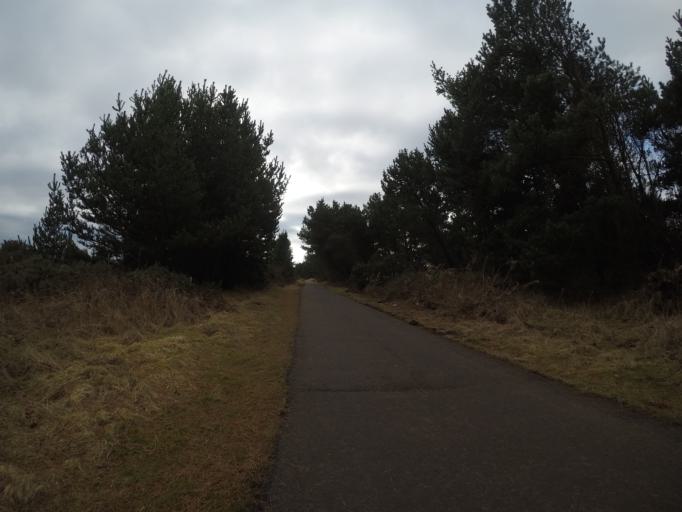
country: GB
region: Scotland
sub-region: North Ayrshire
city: Irvine
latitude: 55.5962
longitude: -4.6748
